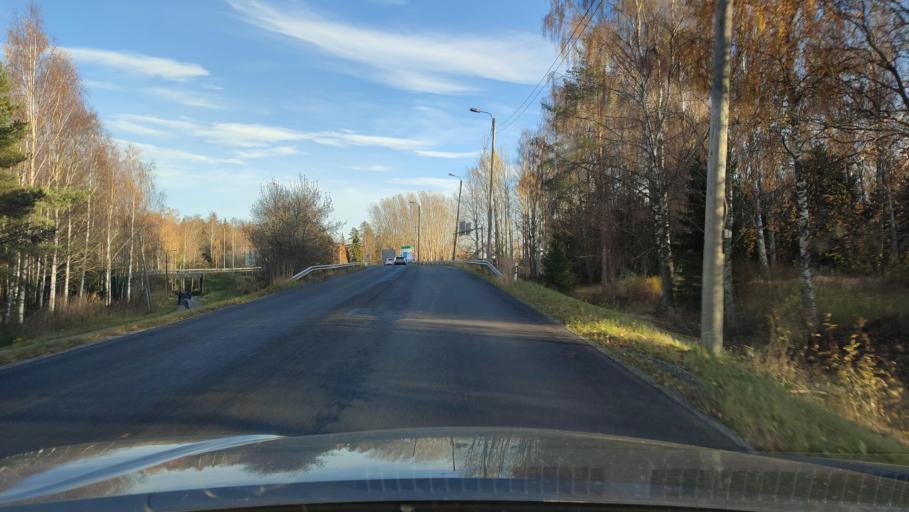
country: FI
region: Ostrobothnia
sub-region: Vaasa
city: Teeriniemi
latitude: 63.0764
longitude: 21.6815
